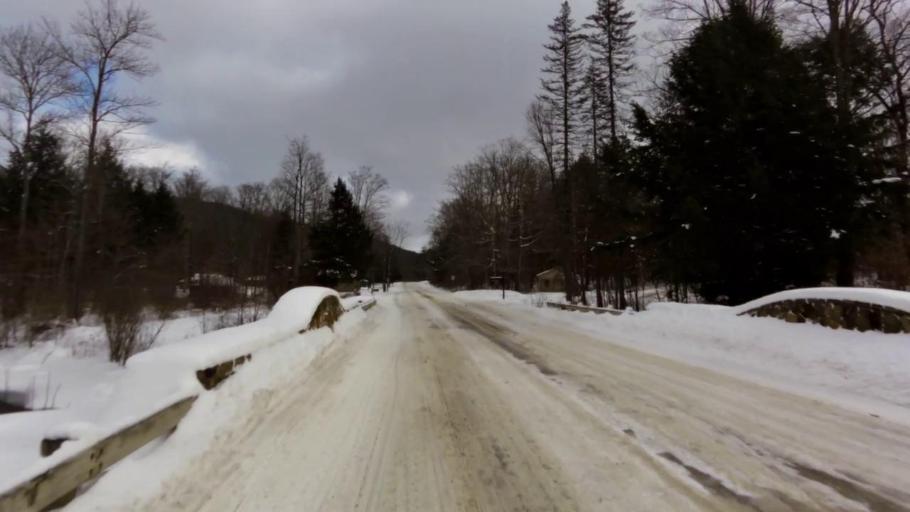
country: US
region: New York
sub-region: Cattaraugus County
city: Salamanca
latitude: 42.0116
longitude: -78.8116
